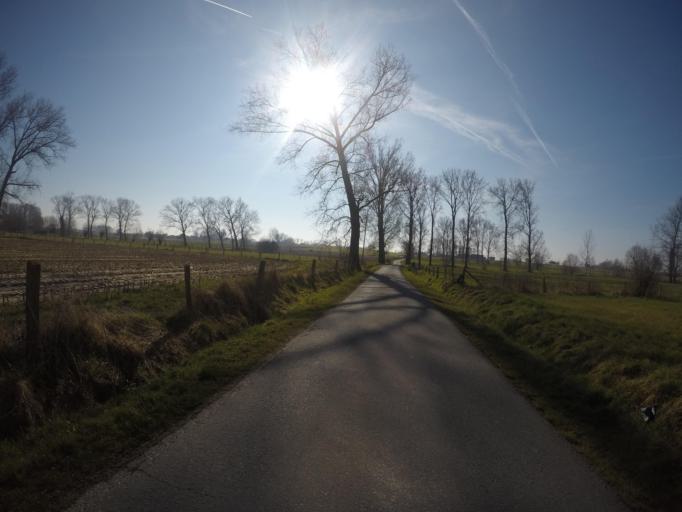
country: BE
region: Flanders
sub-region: Provincie Oost-Vlaanderen
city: Sint-Maria-Lierde
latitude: 50.8072
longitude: 3.7961
